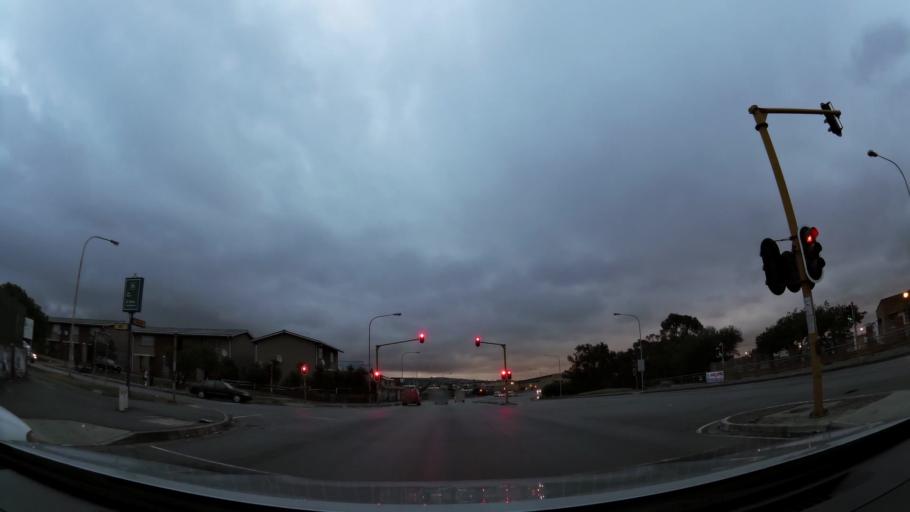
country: ZA
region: Eastern Cape
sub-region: Nelson Mandela Bay Metropolitan Municipality
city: Port Elizabeth
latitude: -33.9250
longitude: 25.5687
